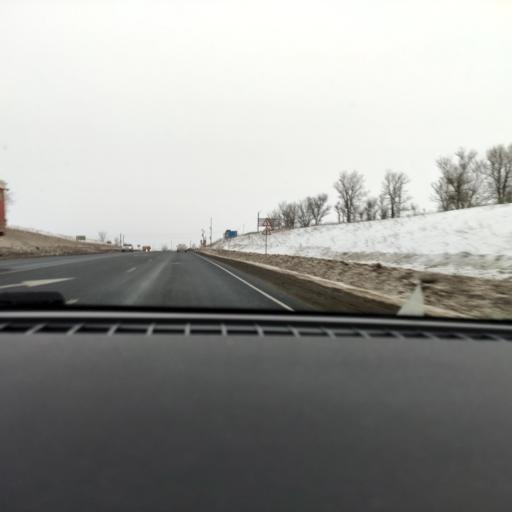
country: RU
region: Samara
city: Novosemeykino
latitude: 53.3926
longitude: 50.4273
